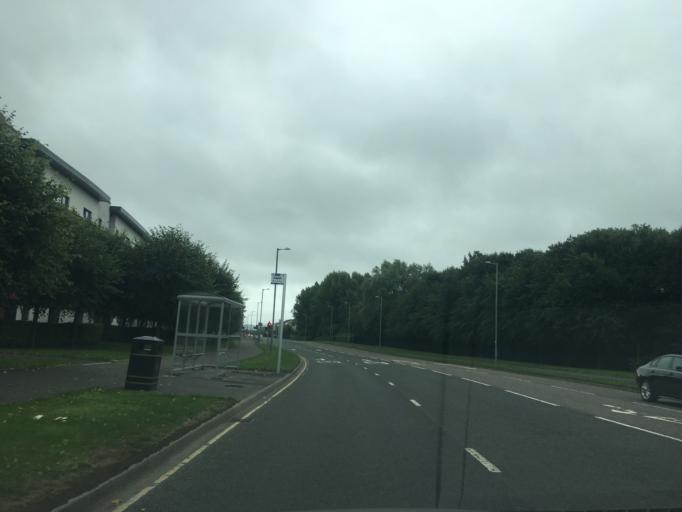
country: GB
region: Scotland
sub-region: Renfrewshire
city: Renfrew
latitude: 55.8827
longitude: -4.3829
